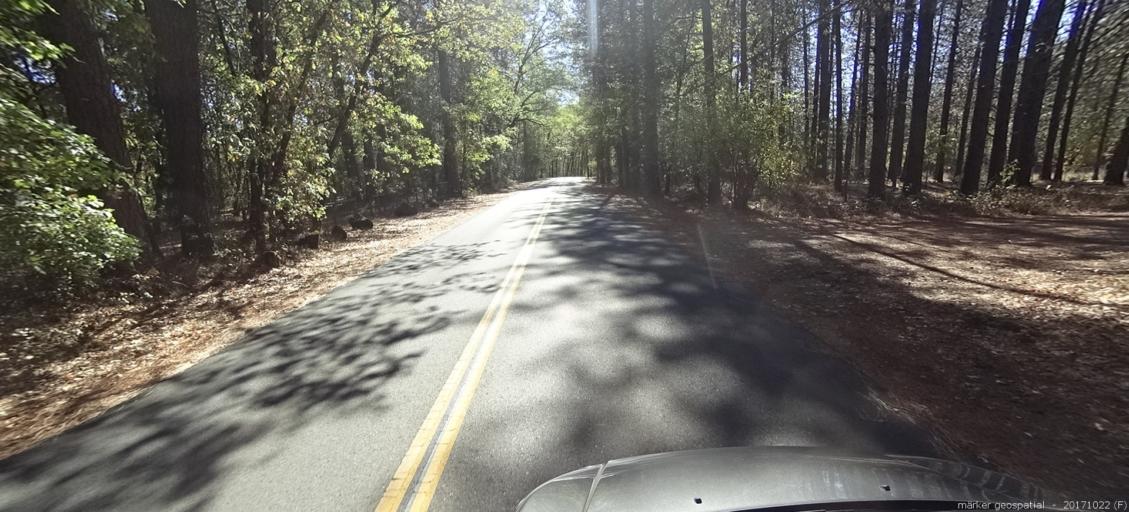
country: US
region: California
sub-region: Shasta County
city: Central Valley (historical)
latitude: 40.8725
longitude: -122.3891
